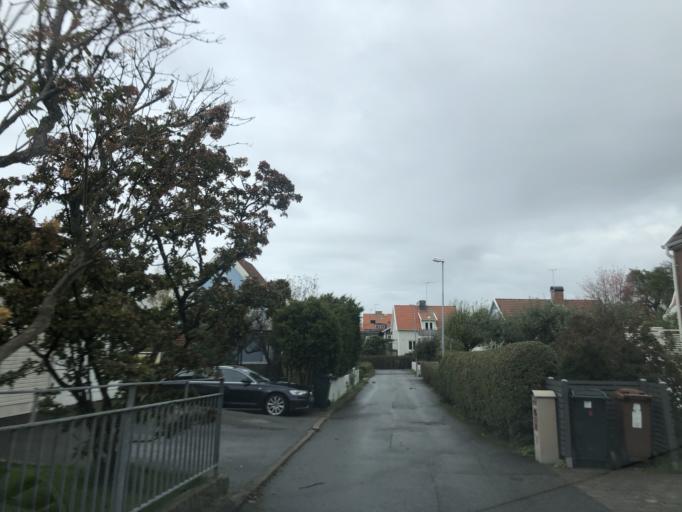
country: SE
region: Vaestra Goetaland
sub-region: Goteborg
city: Majorna
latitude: 57.6741
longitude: 11.8905
